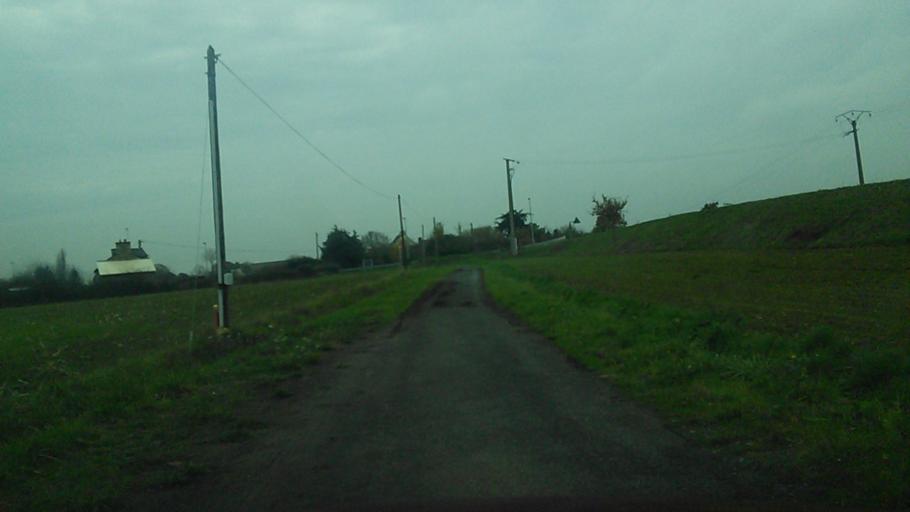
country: FR
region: Brittany
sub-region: Departement des Cotes-d'Armor
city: Yffiniac
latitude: 48.4812
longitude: -2.6567
